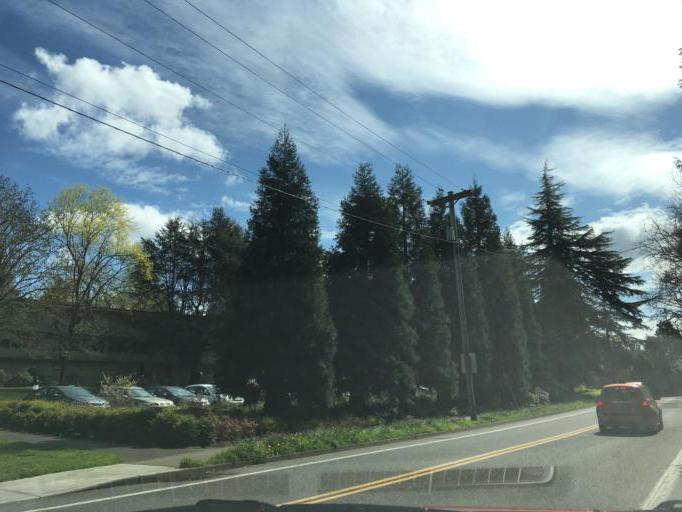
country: US
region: Oregon
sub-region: Clackamas County
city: Milwaukie
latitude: 45.4799
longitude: -122.6351
